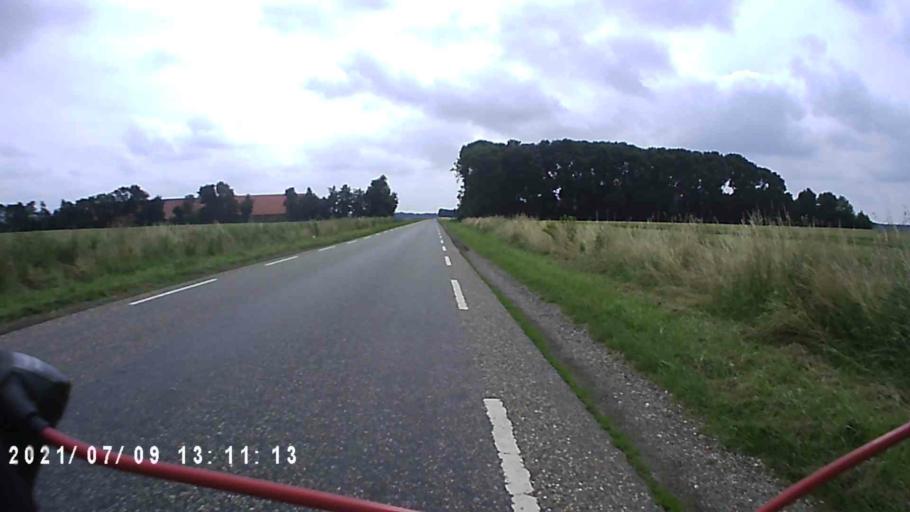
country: NL
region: Groningen
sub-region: Gemeente  Oldambt
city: Winschoten
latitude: 53.1264
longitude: 7.1290
